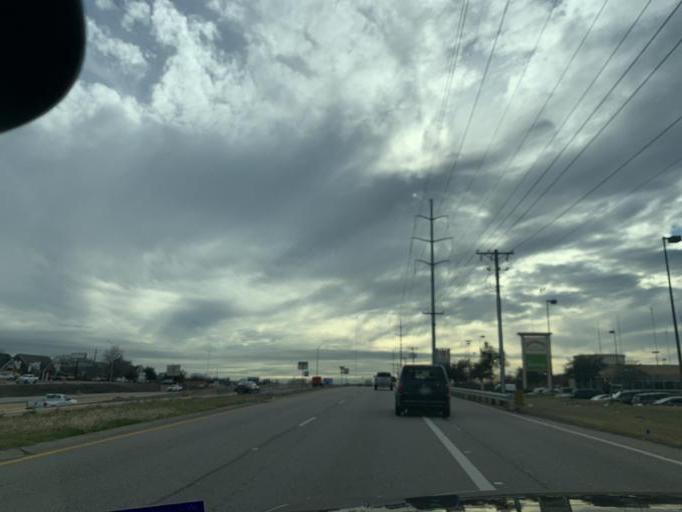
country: US
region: Texas
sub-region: Dallas County
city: Cedar Hill
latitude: 32.6031
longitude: -96.9333
